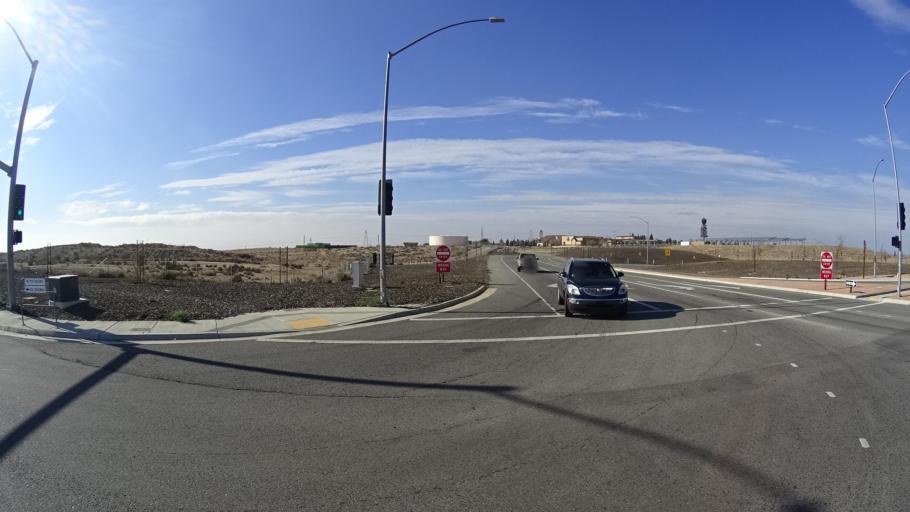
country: US
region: California
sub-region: Kern County
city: Bakersfield
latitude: 35.3954
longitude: -118.9133
